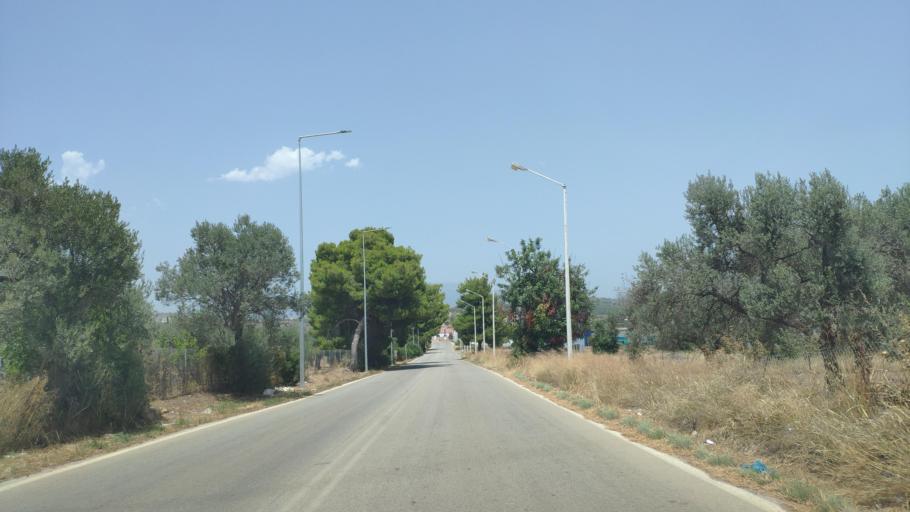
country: GR
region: Peloponnese
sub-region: Nomos Argolidos
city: Porto Cheli
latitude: 37.3397
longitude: 23.1564
